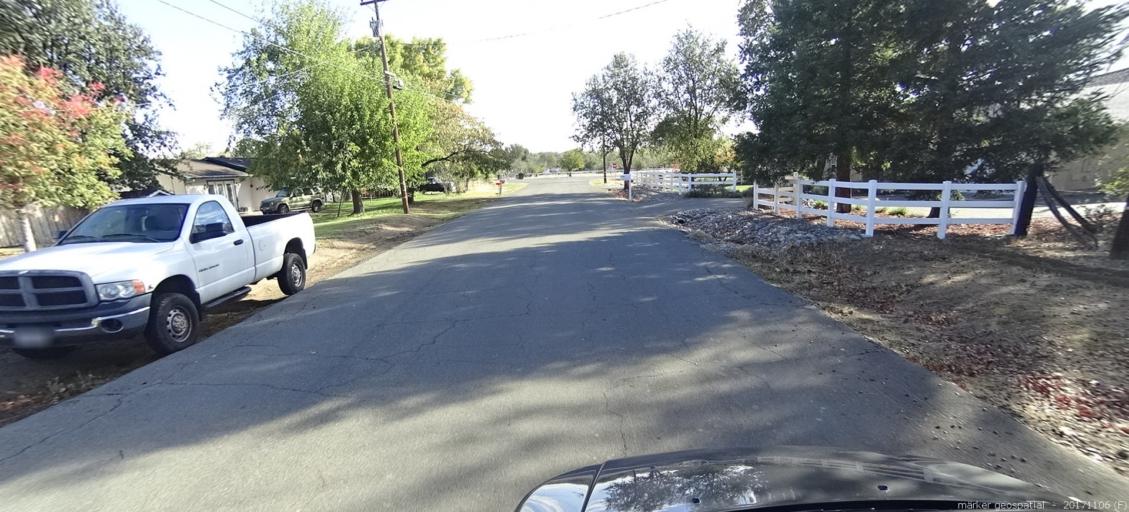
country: US
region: California
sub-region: Shasta County
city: Palo Cedro
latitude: 40.5433
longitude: -122.2399
